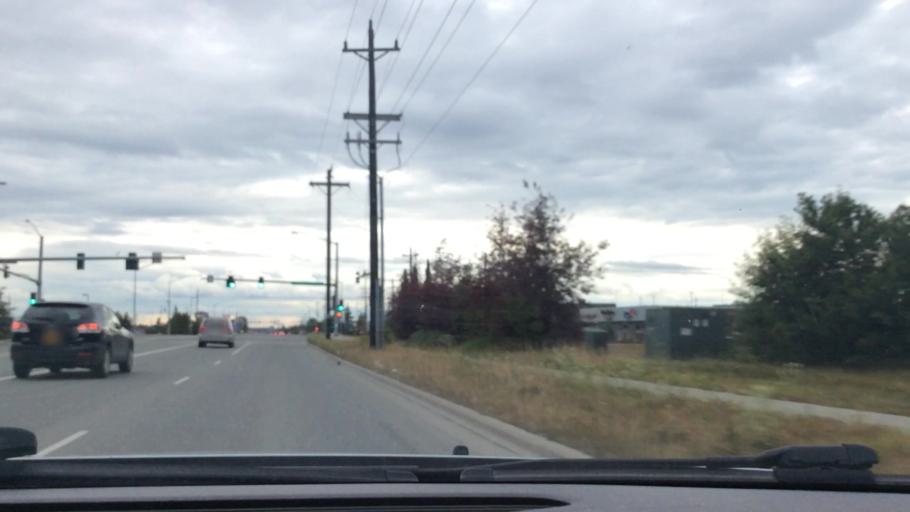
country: US
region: Alaska
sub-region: Anchorage Municipality
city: Anchorage
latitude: 61.1188
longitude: -149.8639
